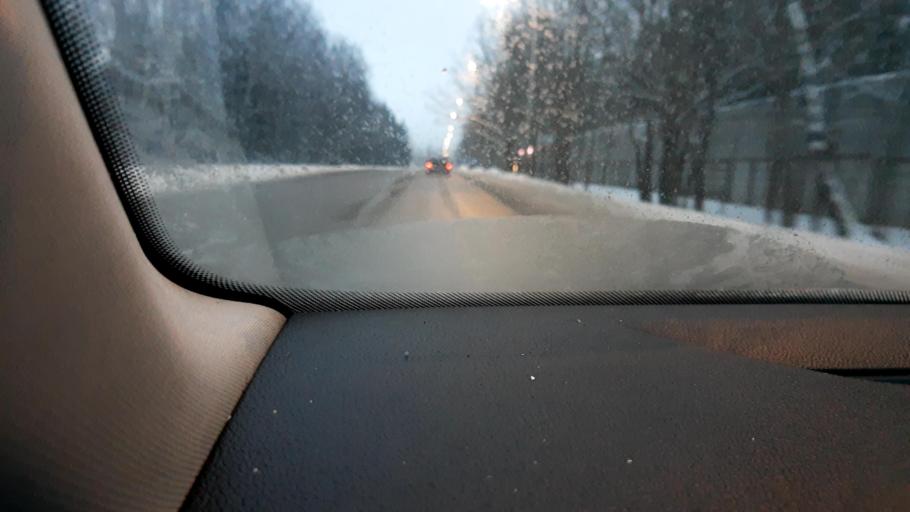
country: RU
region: Moskovskaya
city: Troitsk
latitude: 55.3033
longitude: 37.1973
